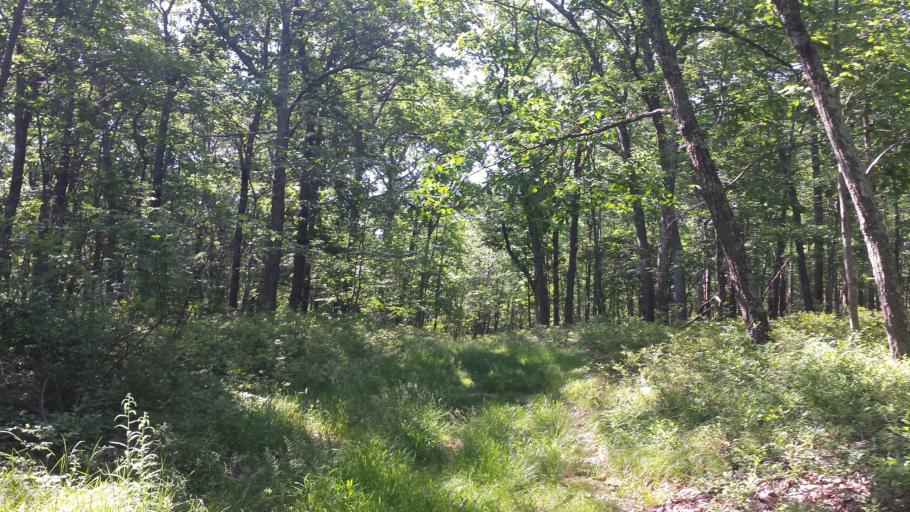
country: US
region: New York
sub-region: Westchester County
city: Pound Ridge
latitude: 41.2517
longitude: -73.5766
